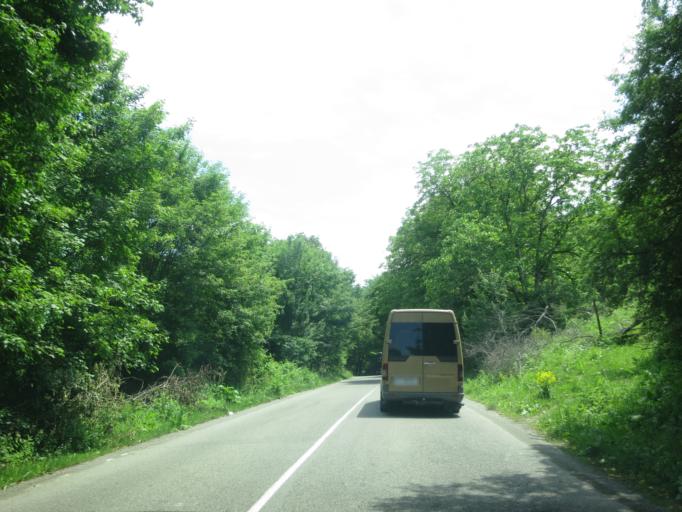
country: GE
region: Kakheti
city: Sagarejo
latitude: 41.8640
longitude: 45.3273
